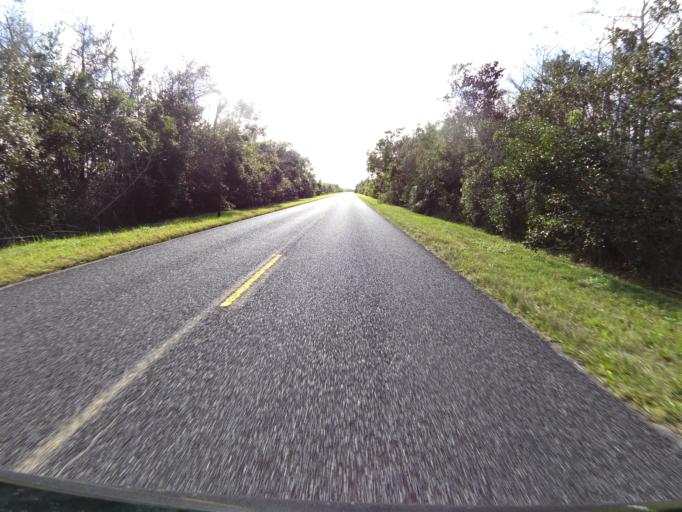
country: US
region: Florida
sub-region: Miami-Dade County
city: Florida City
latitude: 25.4180
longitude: -80.7793
